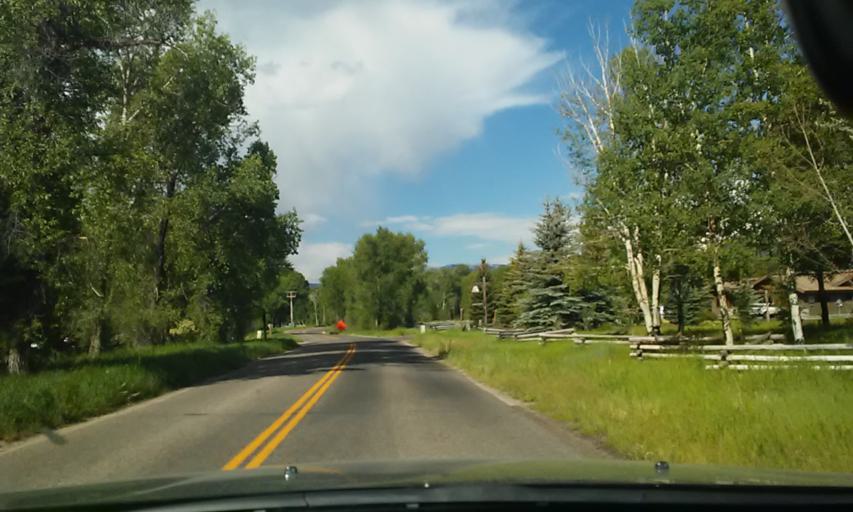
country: US
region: Wyoming
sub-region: Teton County
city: Jackson
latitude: 43.5630
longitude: -110.7532
